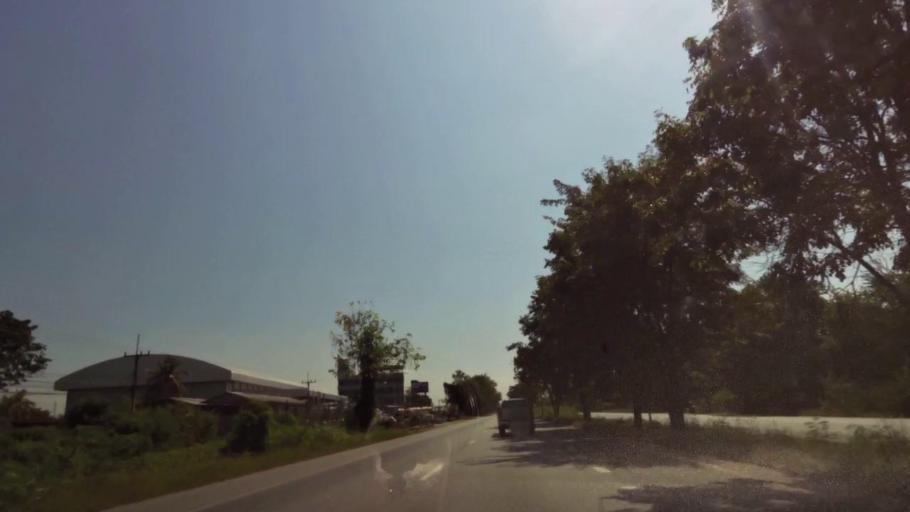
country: TH
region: Nakhon Sawan
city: Kao Liao
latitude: 15.8382
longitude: 100.1175
